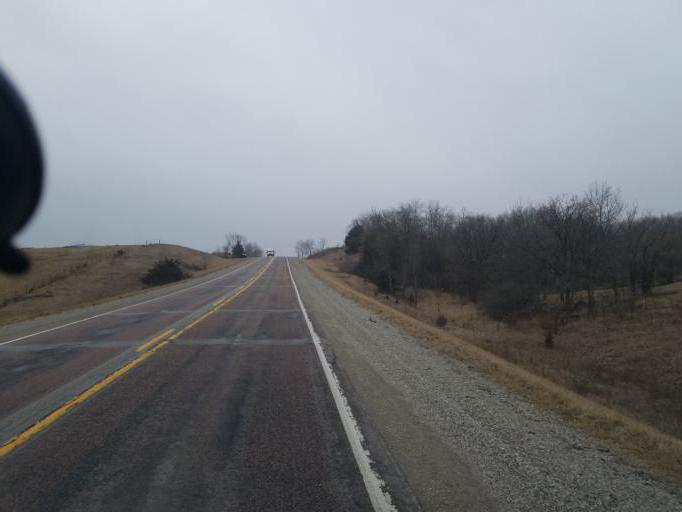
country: US
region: Iowa
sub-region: Appanoose County
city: Centerville
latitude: 40.6239
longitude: -92.9488
